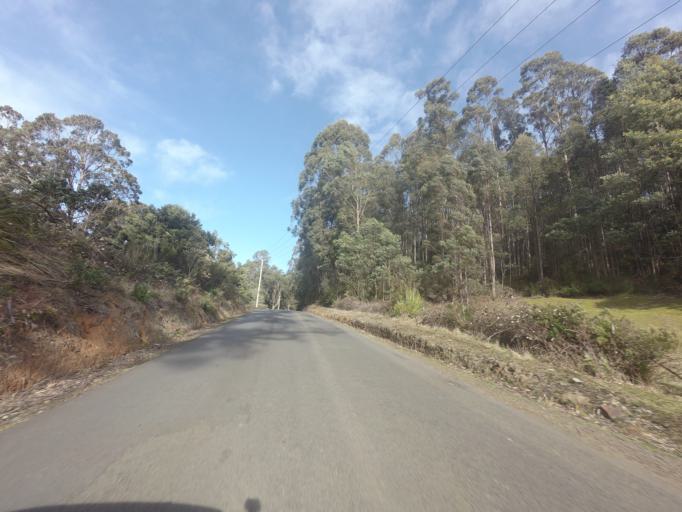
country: AU
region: Tasmania
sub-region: Kingborough
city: Margate
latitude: -43.0098
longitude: 147.1666
